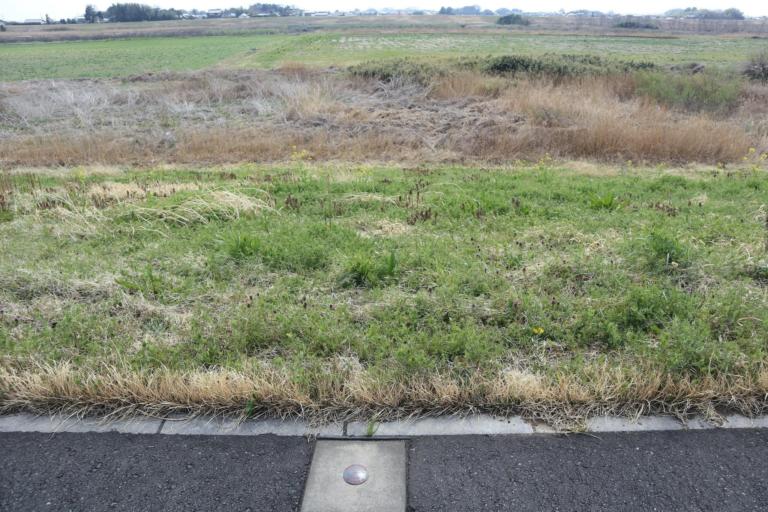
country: JP
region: Tochigi
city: Fujioka
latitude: 36.2750
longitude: 139.6263
